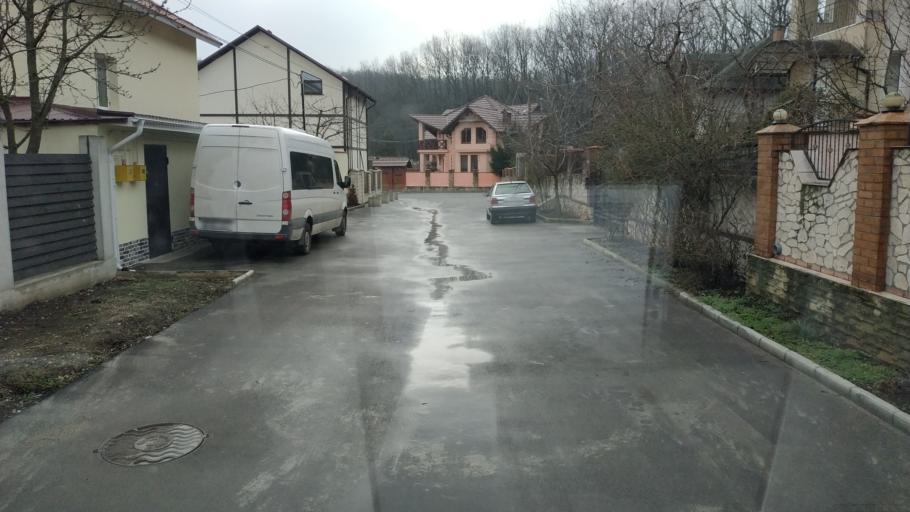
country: MD
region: Chisinau
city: Vatra
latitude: 47.0326
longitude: 28.7559
